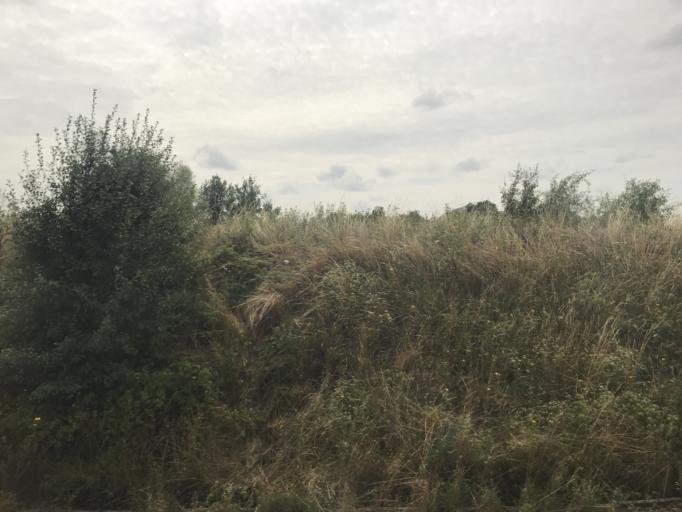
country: PL
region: Kujawsko-Pomorskie
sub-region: Powiat inowroclawski
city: Janikowo
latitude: 52.7290
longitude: 18.0738
